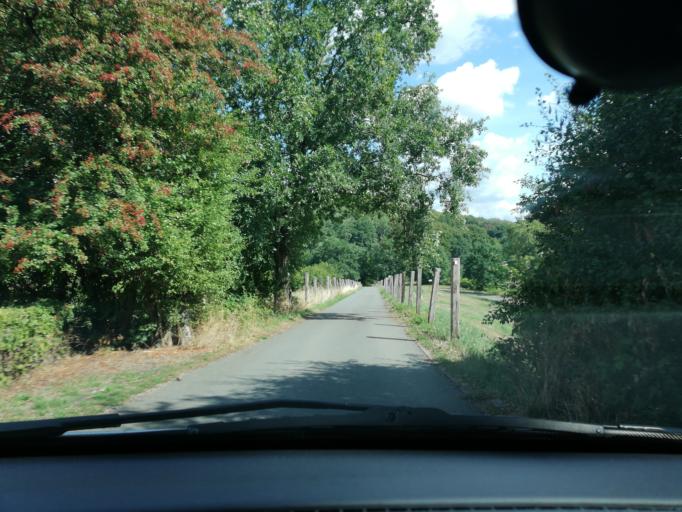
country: DE
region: North Rhine-Westphalia
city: Wetter (Ruhr)
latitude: 51.3758
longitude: 7.3505
